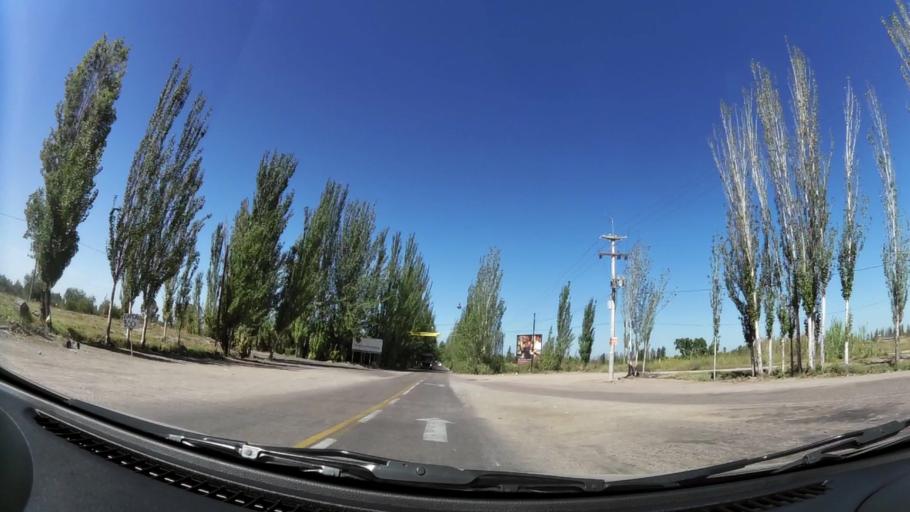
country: AR
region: Mendoza
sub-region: Departamento de Godoy Cruz
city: Godoy Cruz
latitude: -32.9850
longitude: -68.8473
